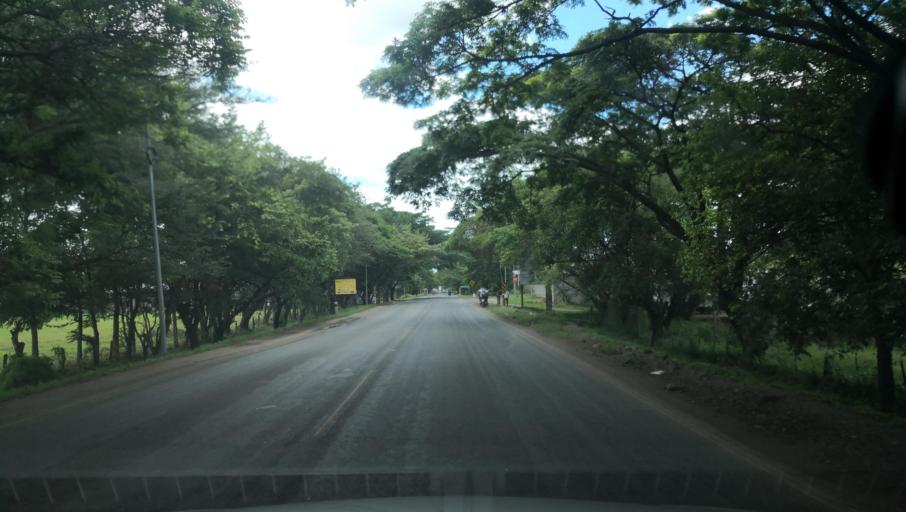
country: NI
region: Esteli
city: Esteli
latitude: 13.1159
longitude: -86.3617
